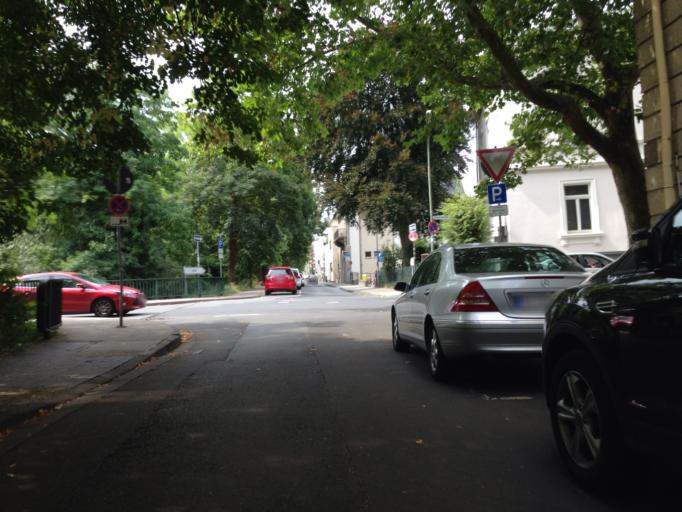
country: DE
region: Hesse
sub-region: Regierungsbezirk Giessen
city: Giessen
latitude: 50.5826
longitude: 8.6777
